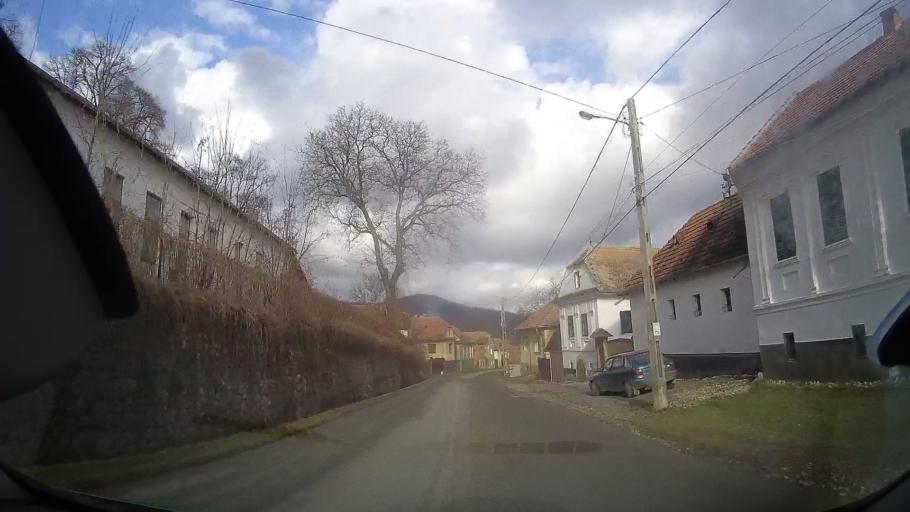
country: RO
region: Alba
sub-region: Comuna Rimetea
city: Rimetea
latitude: 46.4553
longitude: 23.5684
